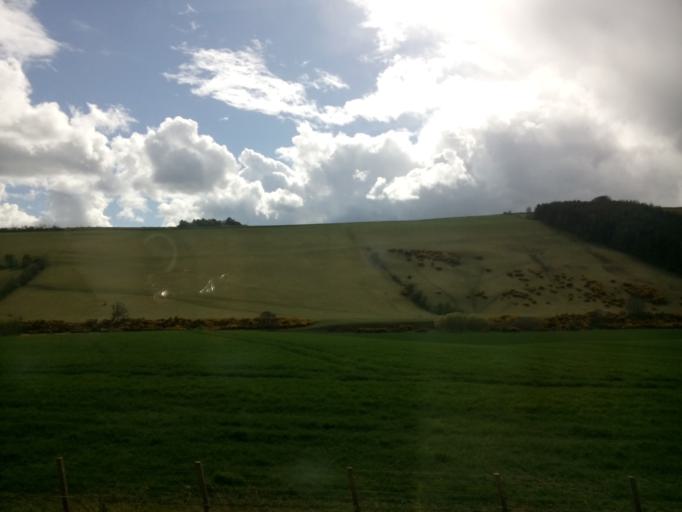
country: GB
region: Scotland
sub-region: The Scottish Borders
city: Chirnside
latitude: 55.8590
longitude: -2.2427
